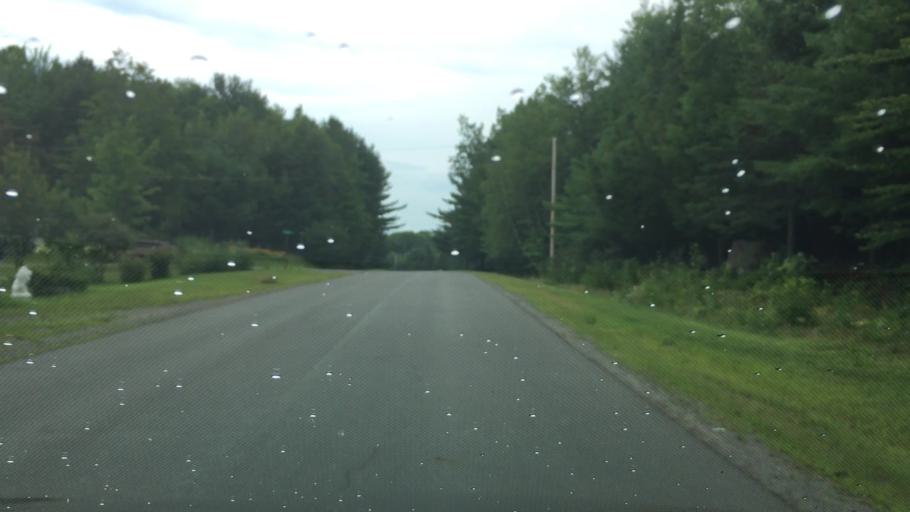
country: US
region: Maine
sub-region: Penobscot County
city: Medway
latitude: 45.6110
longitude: -68.5285
